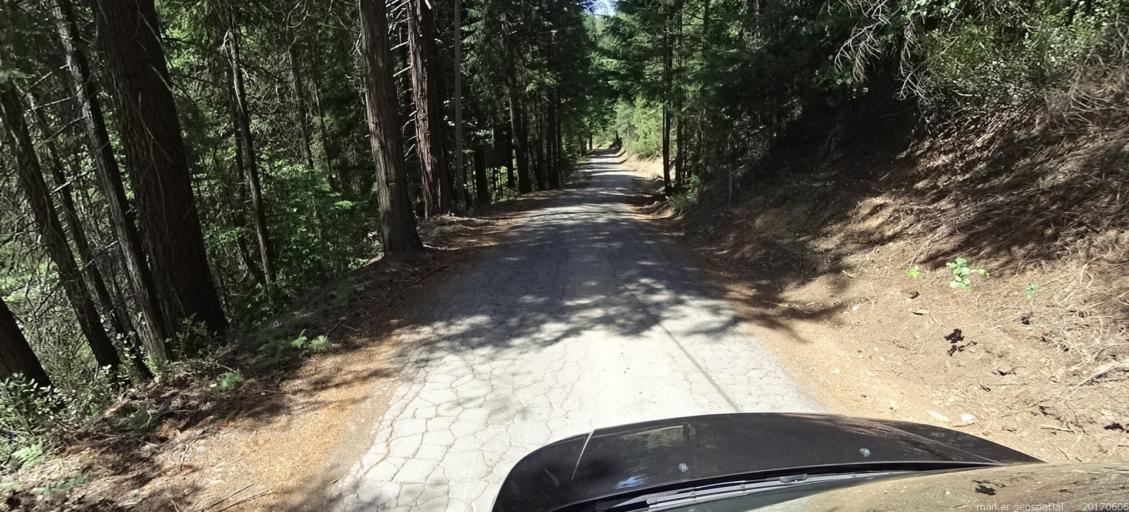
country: US
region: California
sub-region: Siskiyou County
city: Mount Shasta
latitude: 41.2721
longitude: -122.2852
